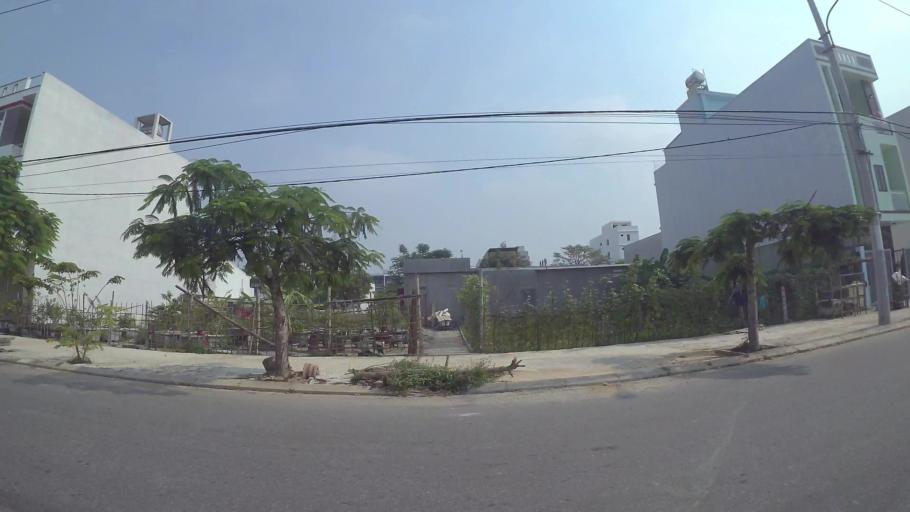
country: VN
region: Da Nang
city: Cam Le
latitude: 16.0019
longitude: 108.2248
